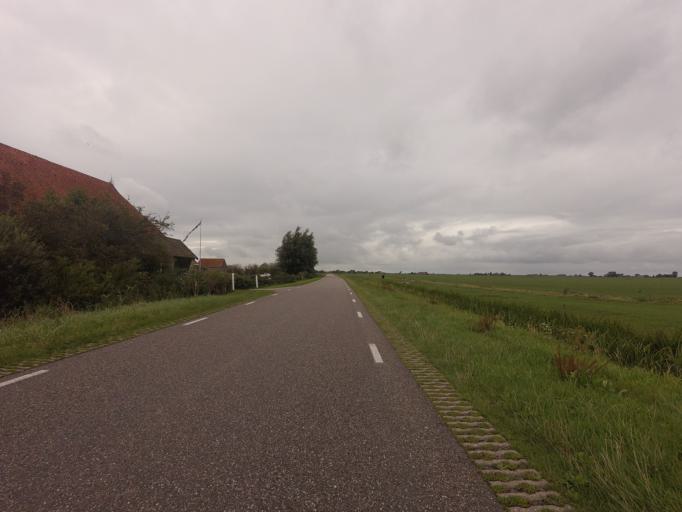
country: NL
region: Friesland
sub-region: Sudwest Fryslan
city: Heeg
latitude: 52.9690
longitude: 5.5622
